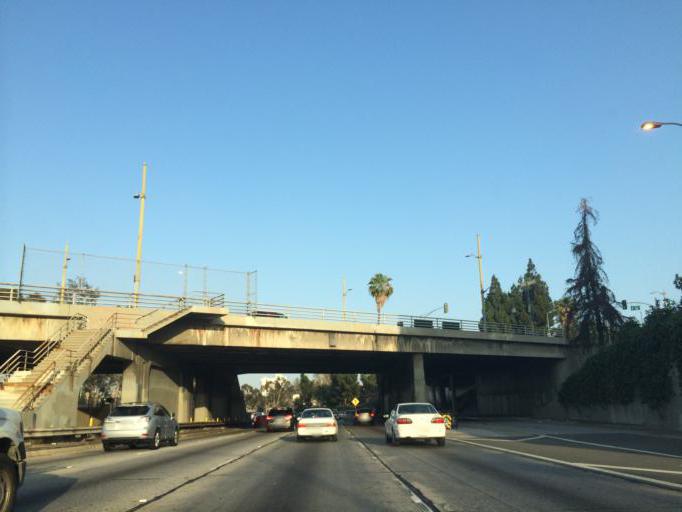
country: US
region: California
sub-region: Los Angeles County
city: Silver Lake
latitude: 34.0797
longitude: -118.2923
